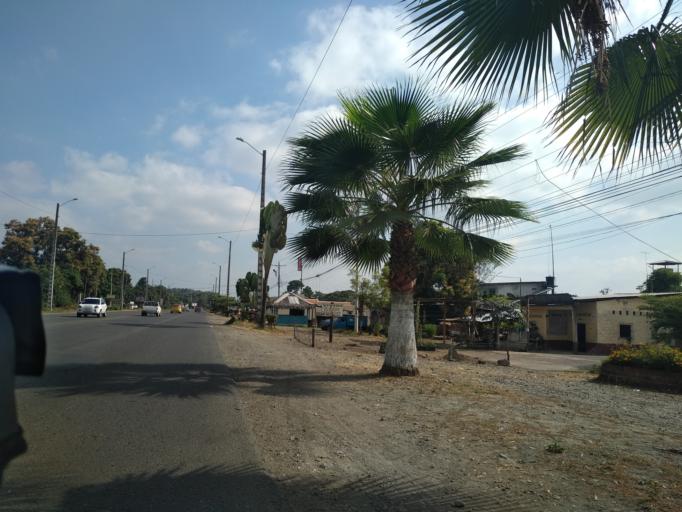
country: EC
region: Los Rios
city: Quevedo
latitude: -1.0629
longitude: -79.4911
